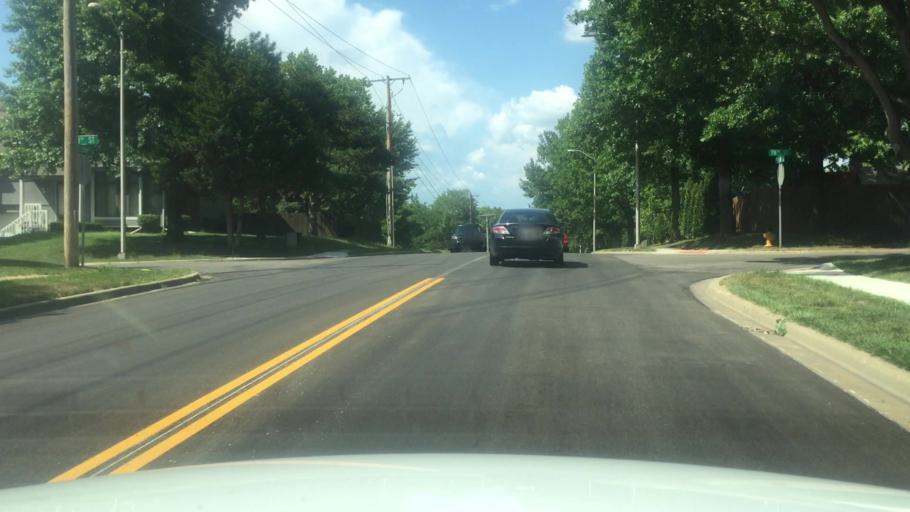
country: US
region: Kansas
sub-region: Johnson County
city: Lenexa
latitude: 38.9878
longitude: -94.7423
